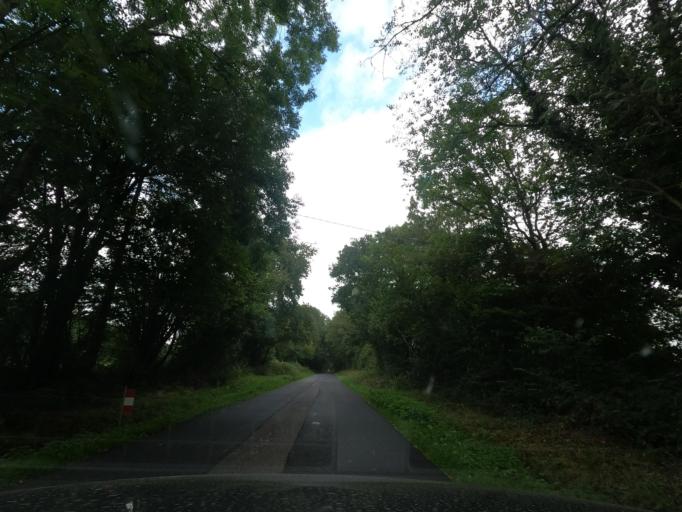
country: FR
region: Lower Normandy
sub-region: Departement de l'Orne
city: Briouze
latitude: 48.7265
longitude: -0.3449
